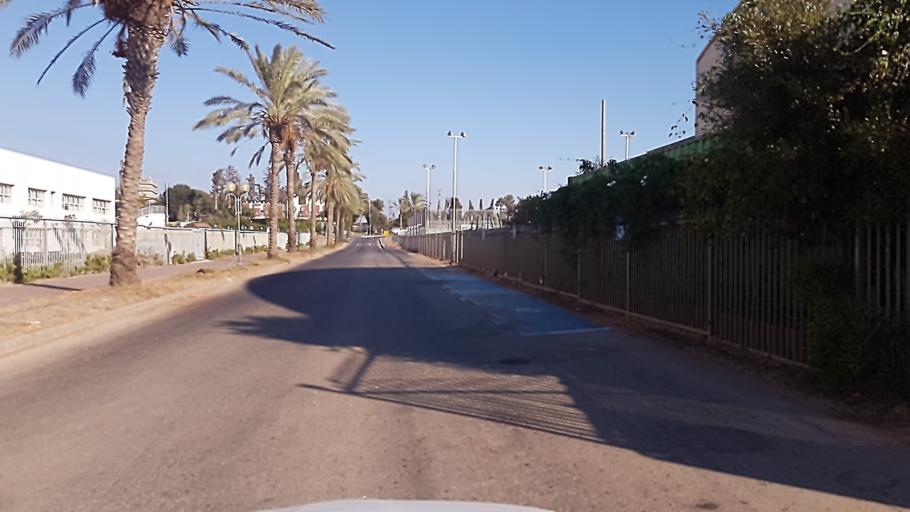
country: IL
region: Central District
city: Kfar Saba
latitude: 32.2004
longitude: 34.9208
